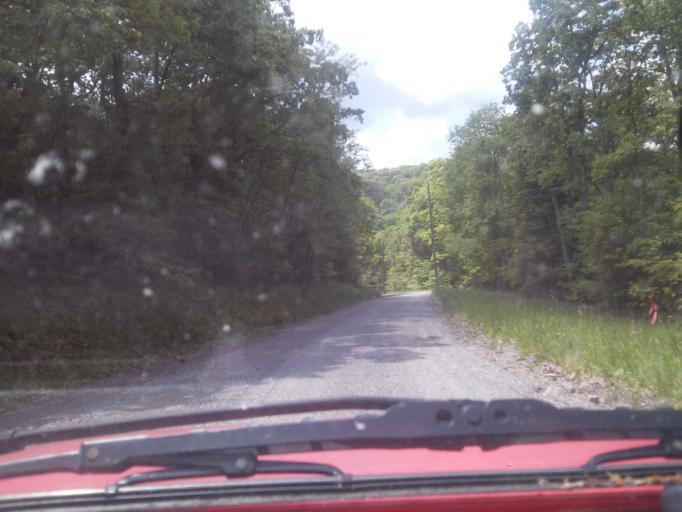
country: US
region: Virginia
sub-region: Giles County
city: Pembroke
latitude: 37.3665
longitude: -80.5340
